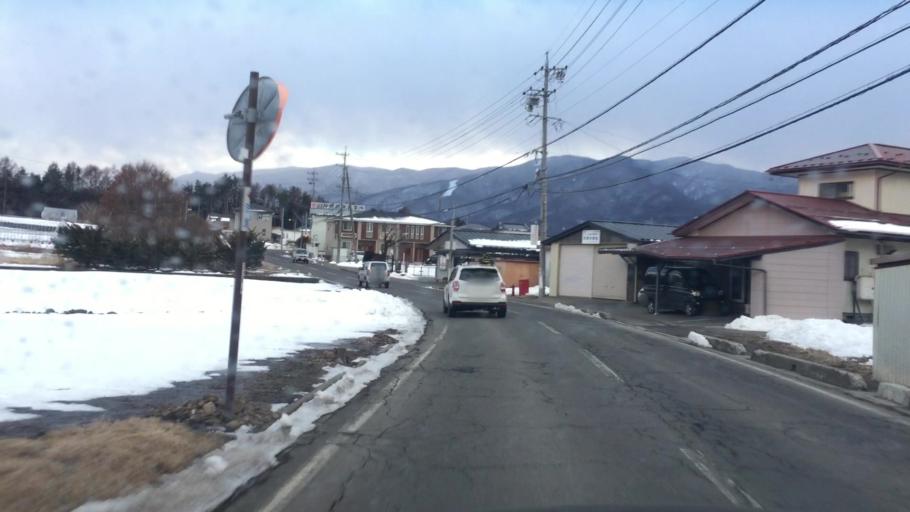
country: JP
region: Nagano
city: Chino
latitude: 35.9578
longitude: 138.2157
